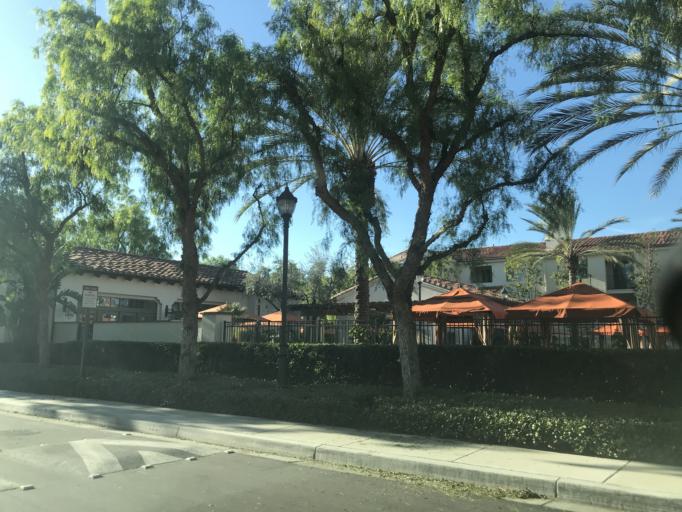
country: US
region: California
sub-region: Orange County
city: Lake Forest
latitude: 33.7023
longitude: -117.7412
